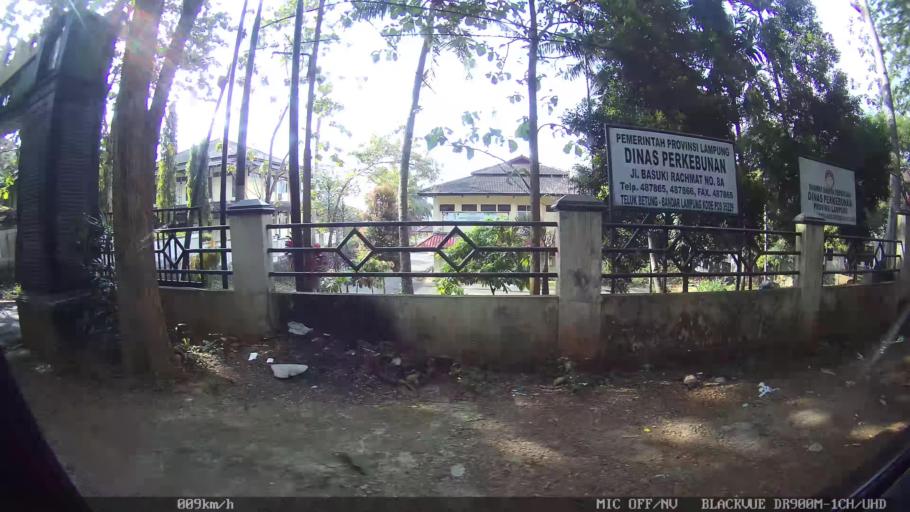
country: ID
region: Lampung
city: Bandarlampung
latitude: -5.4420
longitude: 105.2557
